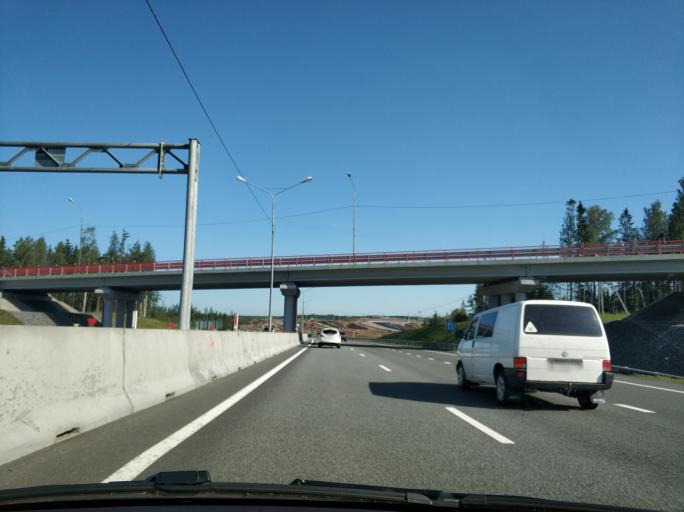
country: RU
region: Leningrad
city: Sosnovo
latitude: 60.5020
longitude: 30.1950
